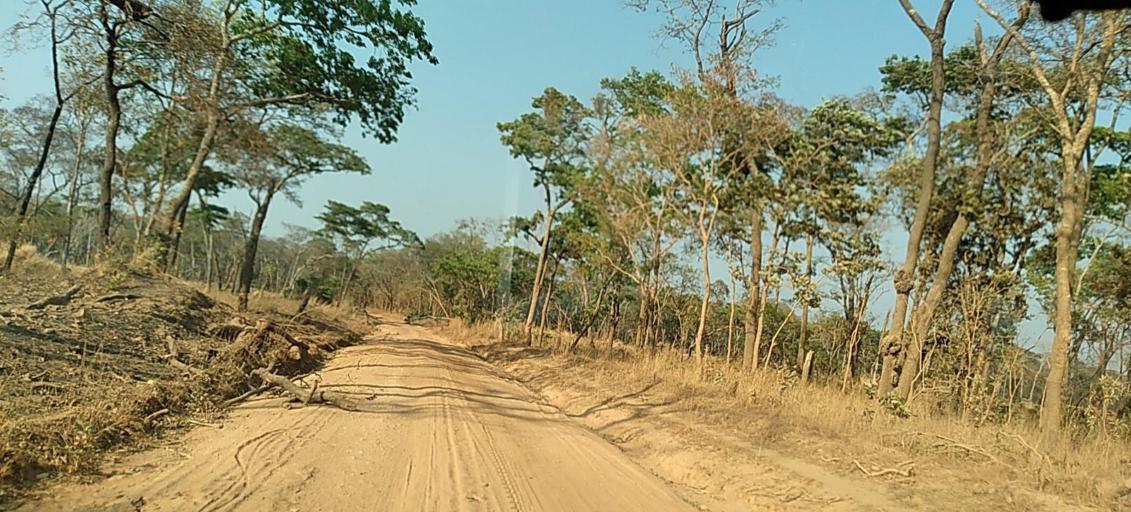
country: ZM
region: North-Western
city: Kasempa
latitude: -13.5733
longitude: 25.9927
